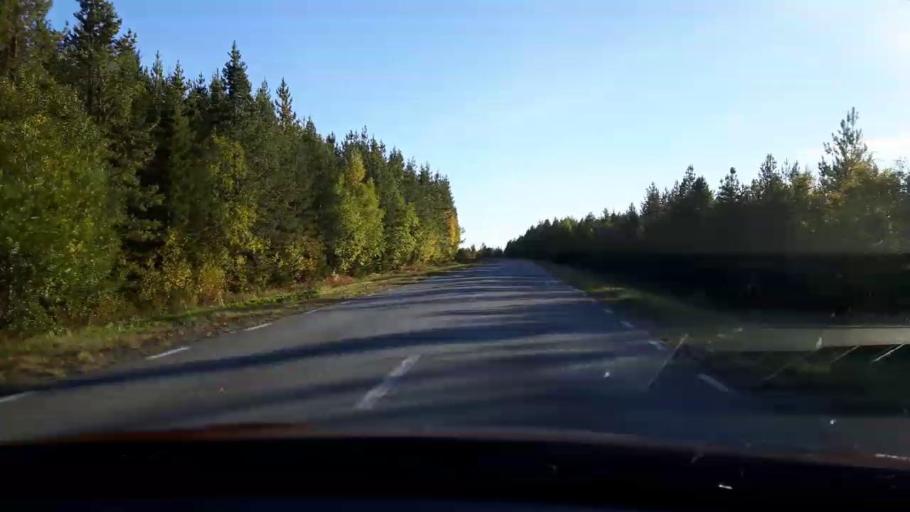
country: SE
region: Jaemtland
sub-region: OEstersunds Kommun
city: Lit
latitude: 63.7599
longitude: 14.7187
